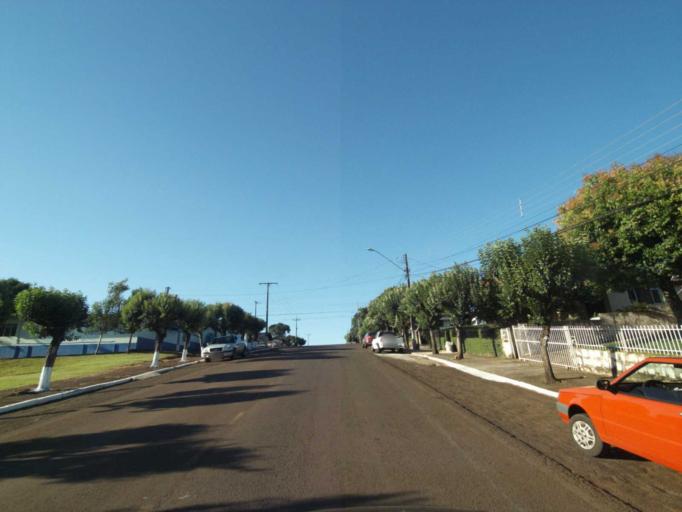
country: BR
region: Parana
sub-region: Coronel Vivida
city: Coronel Vivida
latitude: -25.9600
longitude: -52.8143
